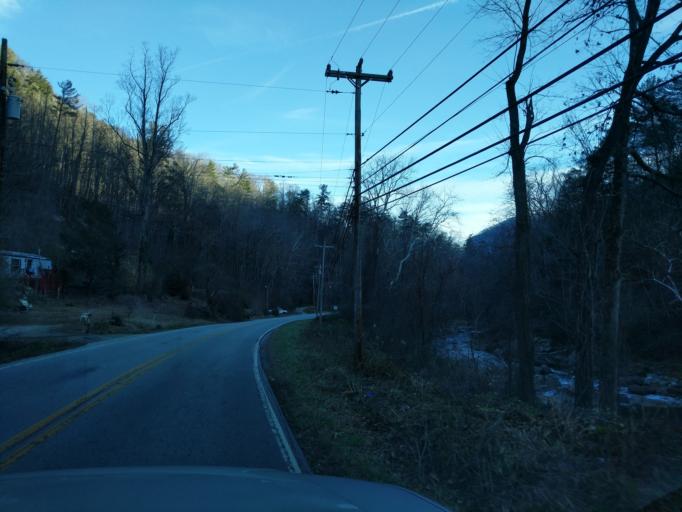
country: US
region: North Carolina
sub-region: Rutherford County
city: Lake Lure
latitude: 35.4492
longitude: -82.2790
